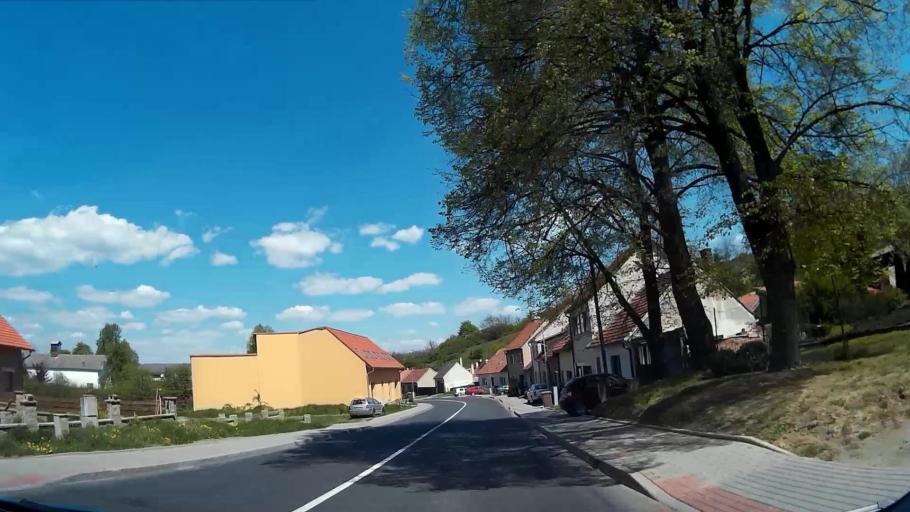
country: CZ
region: South Moravian
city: Ivancice
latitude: 49.1386
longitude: 16.3887
